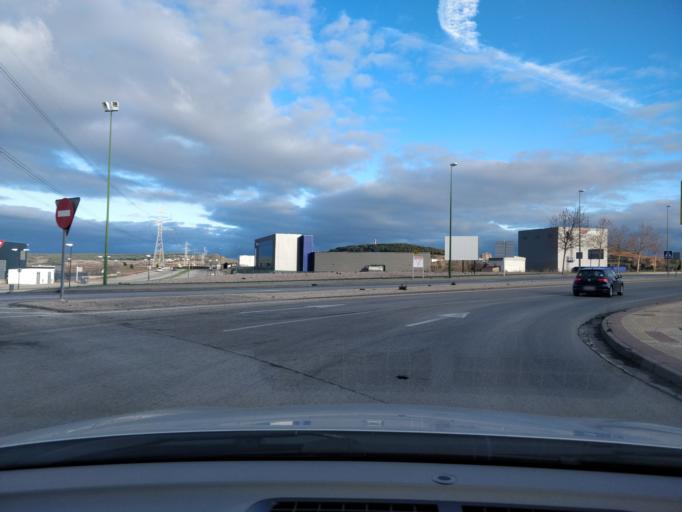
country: ES
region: Castille and Leon
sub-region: Provincia de Burgos
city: Burgos
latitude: 42.3630
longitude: -3.7111
